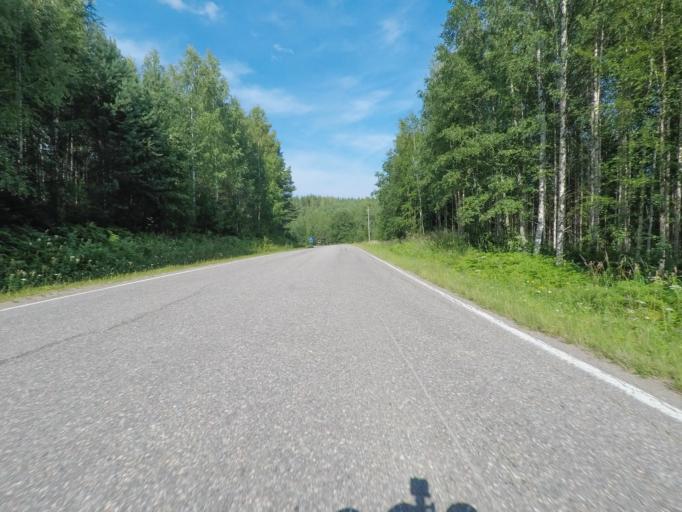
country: FI
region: Southern Savonia
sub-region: Mikkeli
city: Puumala
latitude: 61.6704
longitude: 28.2294
